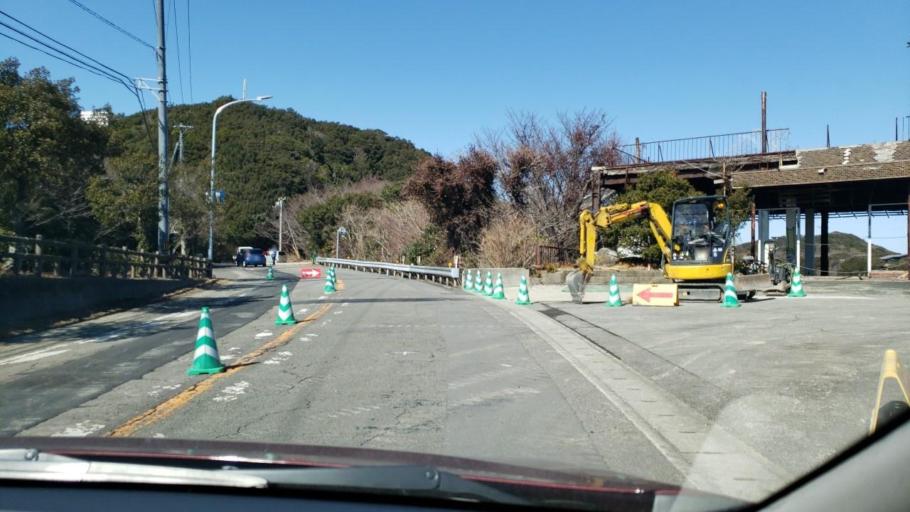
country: JP
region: Tokushima
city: Narutocho-mitsuishi
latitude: 34.2381
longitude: 134.6124
